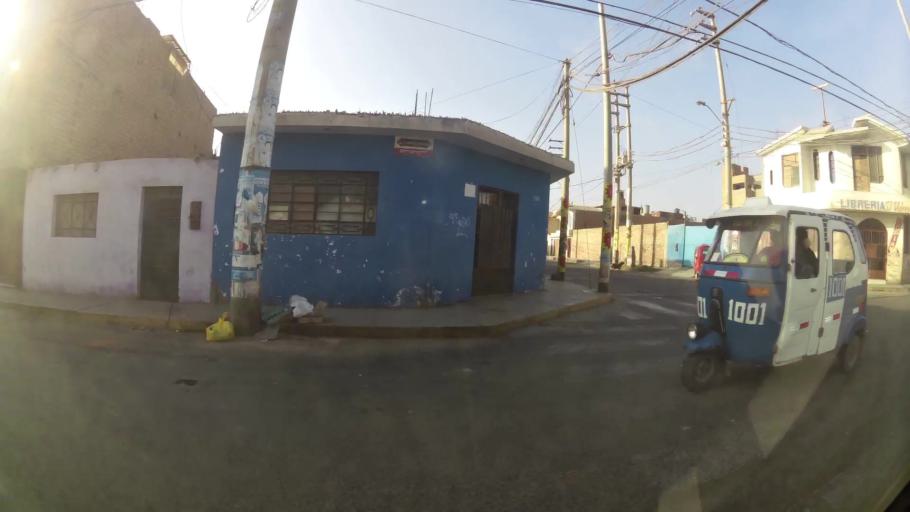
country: PE
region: Lima
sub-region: Huaura
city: Huacho
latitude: -11.1103
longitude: -77.6030
